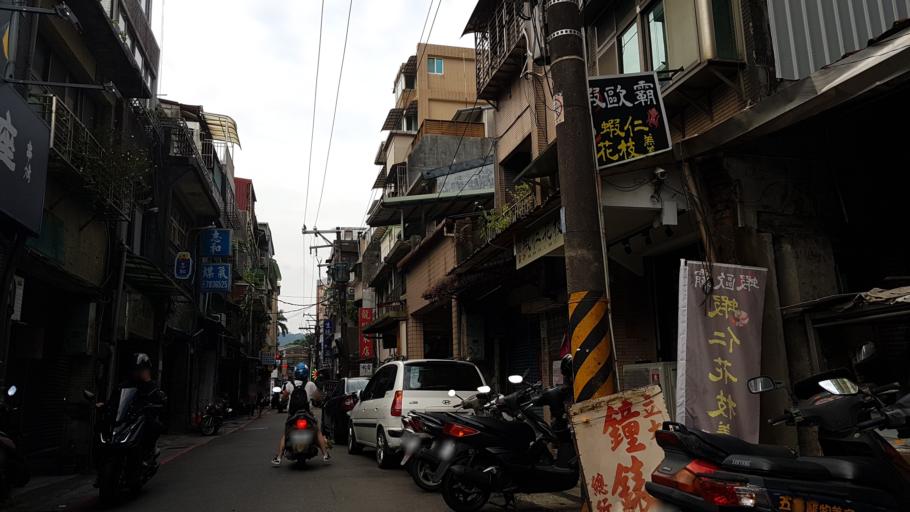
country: TW
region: Taipei
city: Taipei
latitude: 25.0540
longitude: 121.6153
